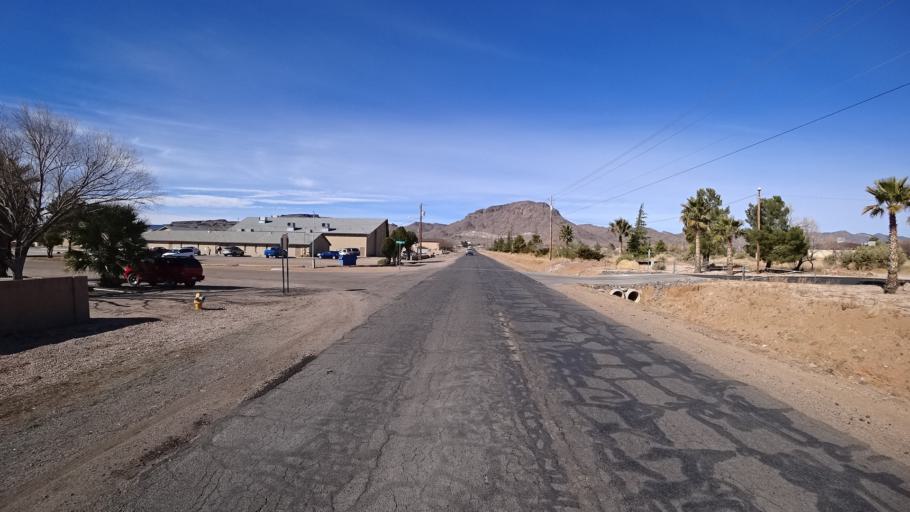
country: US
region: Arizona
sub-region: Mohave County
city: New Kingman-Butler
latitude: 35.2684
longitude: -114.0289
